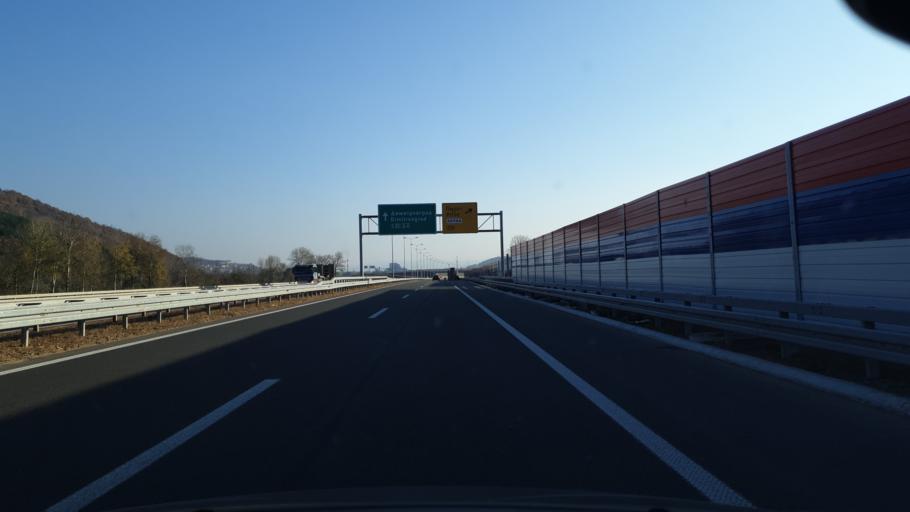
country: RS
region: Central Serbia
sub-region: Pirotski Okrug
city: Pirot
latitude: 43.1955
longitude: 22.5614
